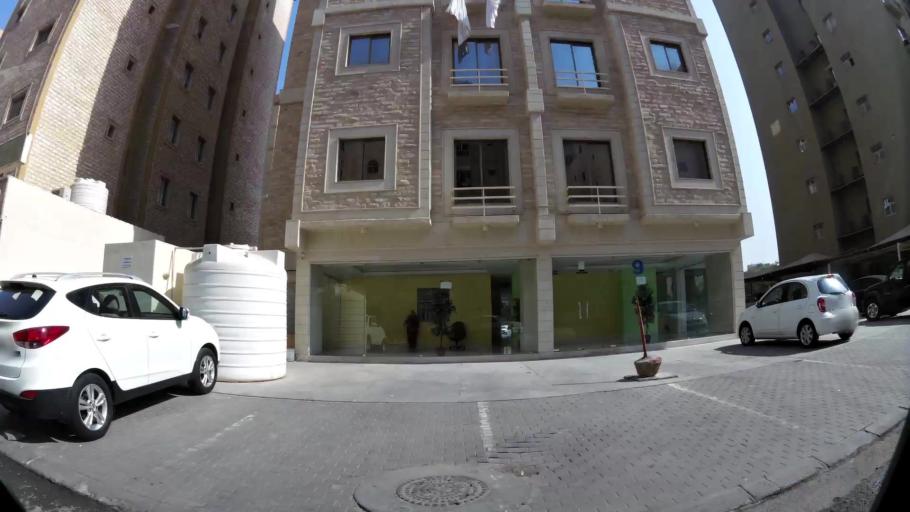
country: KW
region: Muhafazat Hawalli
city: Hawalli
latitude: 29.3359
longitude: 48.0327
